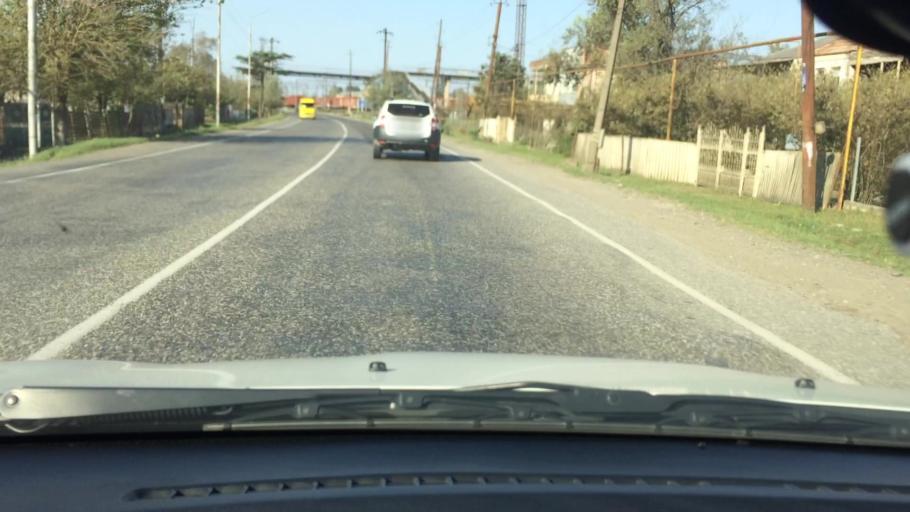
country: GE
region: Imereti
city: Samtredia
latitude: 42.1655
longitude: 42.3672
